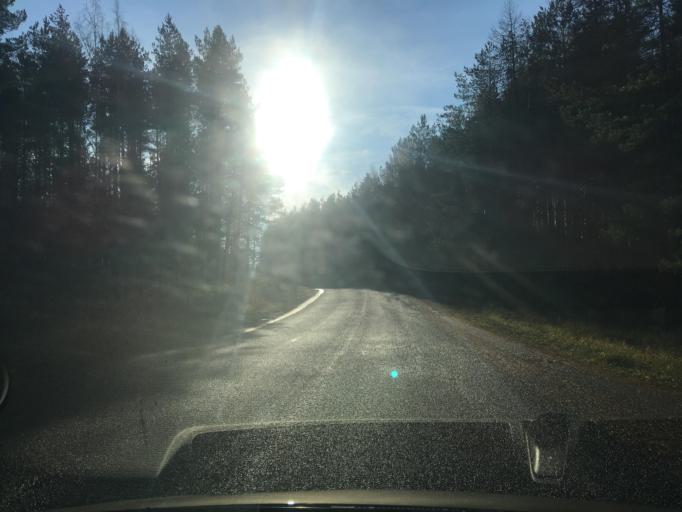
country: EE
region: Harju
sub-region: Maardu linn
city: Maardu
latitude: 59.4704
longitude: 25.0269
